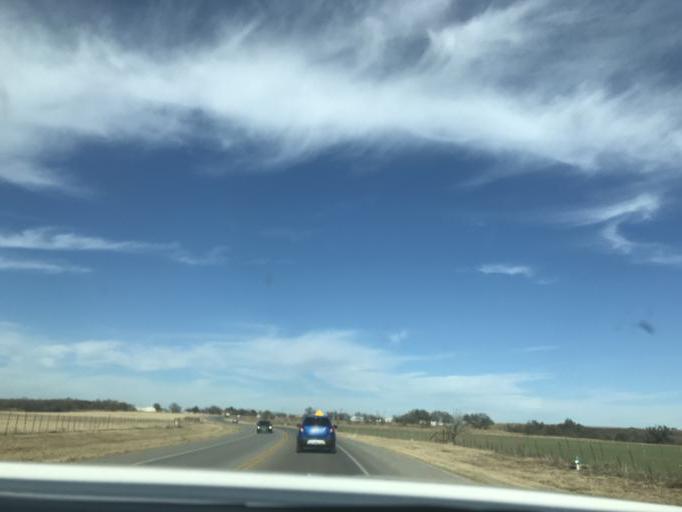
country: US
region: Texas
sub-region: Erath County
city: Stephenville
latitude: 32.2382
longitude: -98.1991
